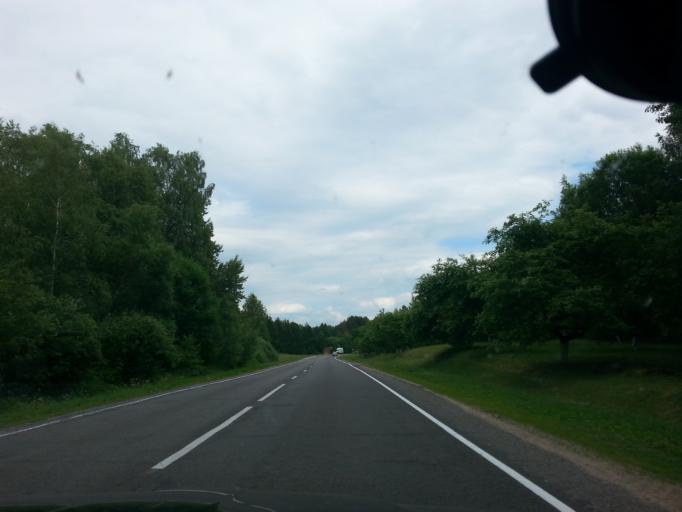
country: BY
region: Minsk
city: Narach
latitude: 54.8893
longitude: 26.7852
